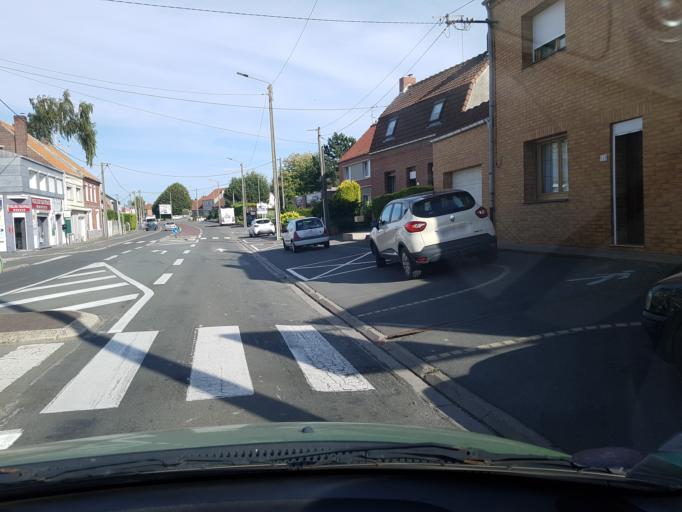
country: FR
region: Nord-Pas-de-Calais
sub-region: Departement du Pas-de-Calais
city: Vendin-les-Bethune
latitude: 50.5398
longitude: 2.6012
